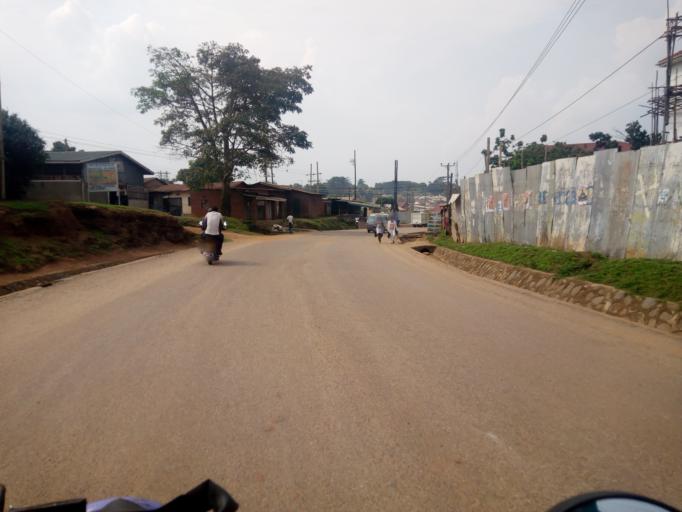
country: UG
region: Central Region
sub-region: Wakiso District
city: Kireka
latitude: 0.3051
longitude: 32.6519
